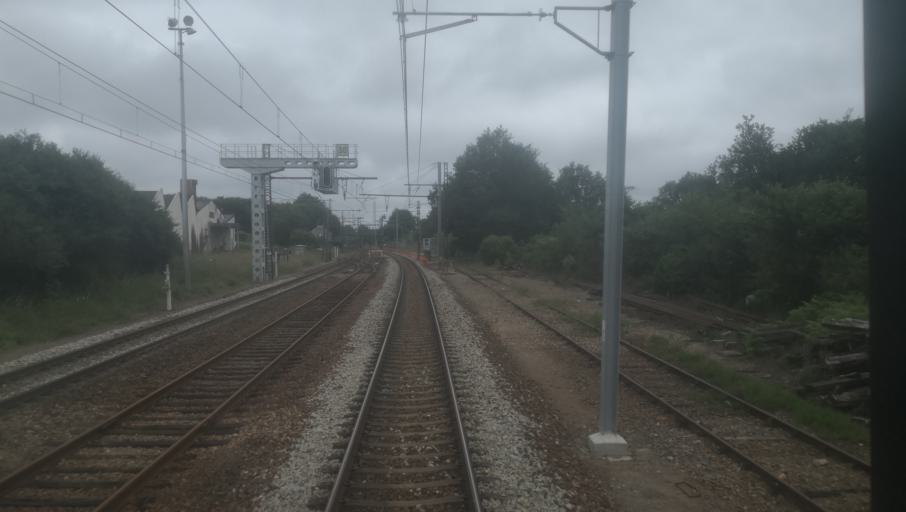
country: FR
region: Limousin
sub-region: Departement de la Creuse
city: La Souterraine
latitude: 46.2453
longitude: 1.4877
